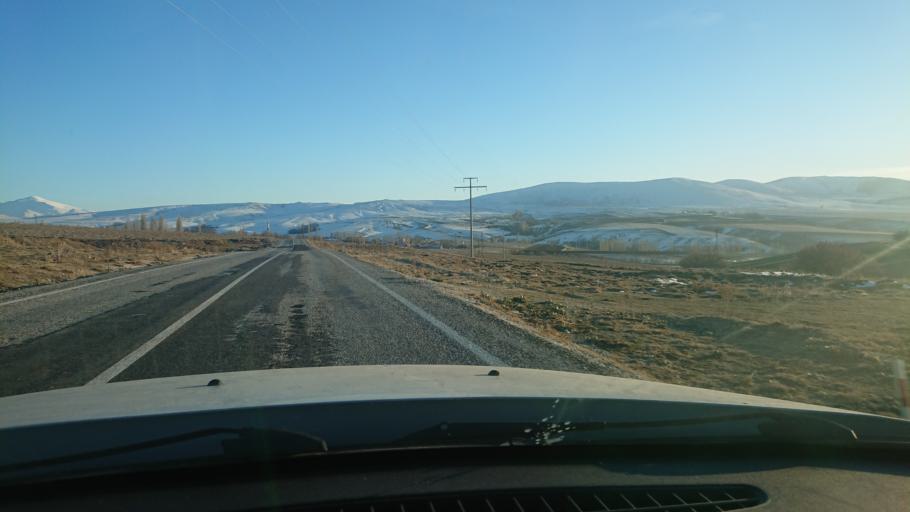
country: TR
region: Aksaray
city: Ortakoy
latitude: 38.7625
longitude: 33.9324
